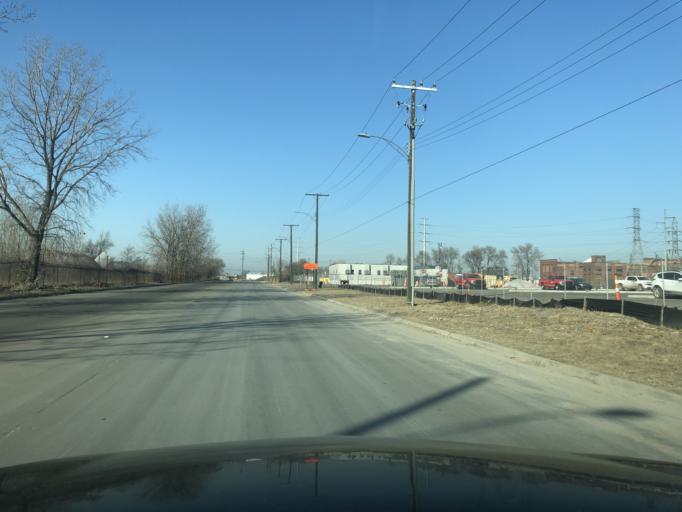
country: US
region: Michigan
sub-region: Wayne County
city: River Rouge
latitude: 42.2937
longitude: -83.1035
